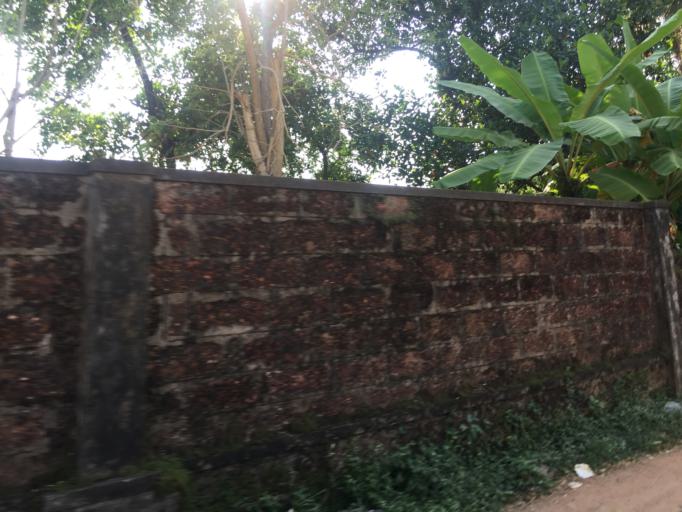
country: IN
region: Karnataka
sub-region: Dakshina Kannada
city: Ullal
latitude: 12.8510
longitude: 74.8447
